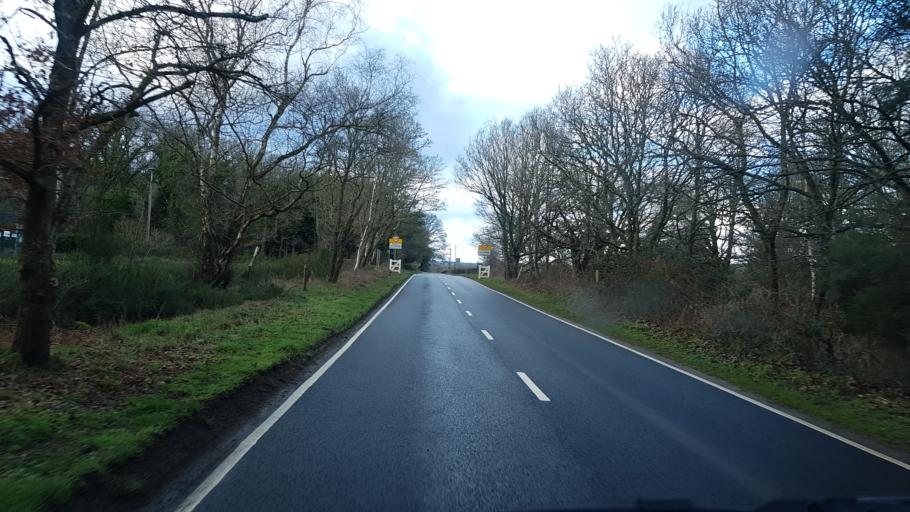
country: GB
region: England
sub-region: Surrey
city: Elstead
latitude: 51.1787
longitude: -0.7500
